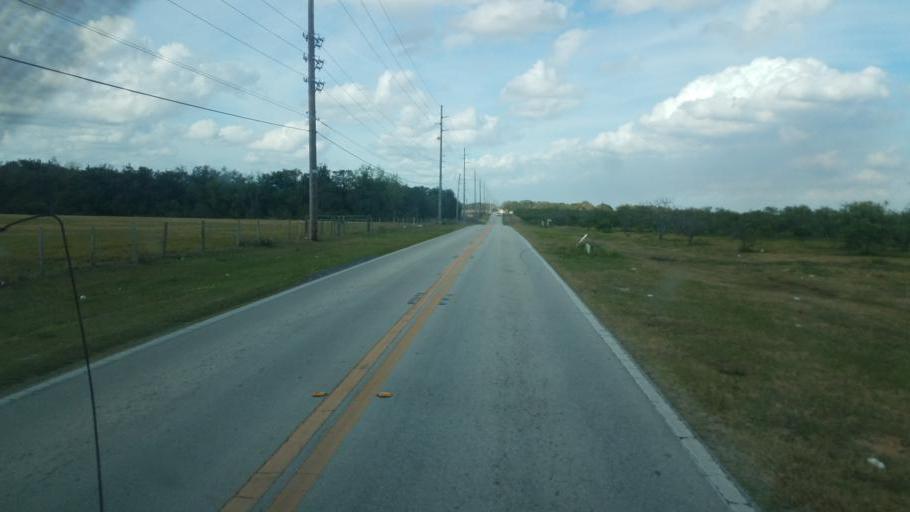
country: US
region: Florida
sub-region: Polk County
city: Haines City
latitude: 28.1218
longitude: -81.5904
